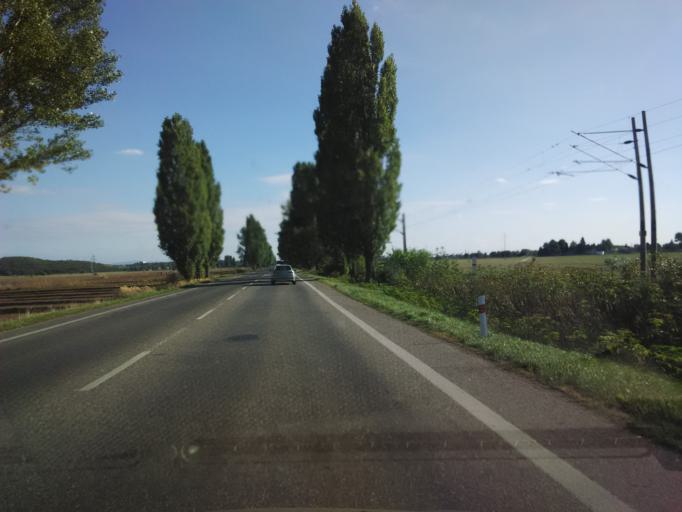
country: SK
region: Nitriansky
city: Levice
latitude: 48.2527
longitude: 18.5787
